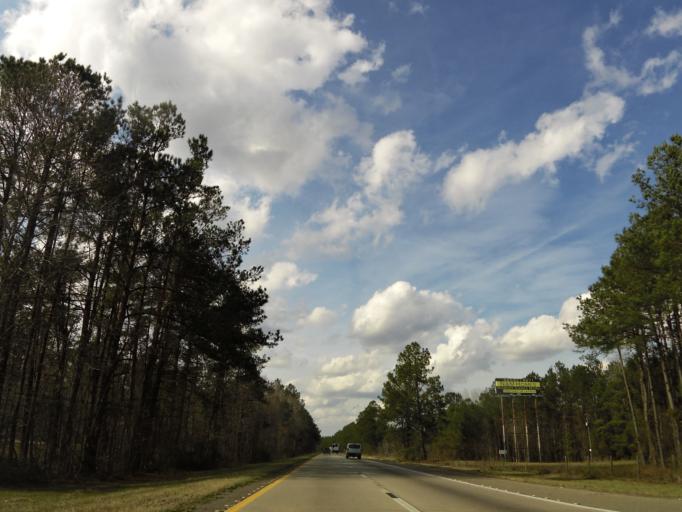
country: US
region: South Carolina
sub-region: Orangeburg County
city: Holly Hill
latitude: 33.2171
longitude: -80.4183
